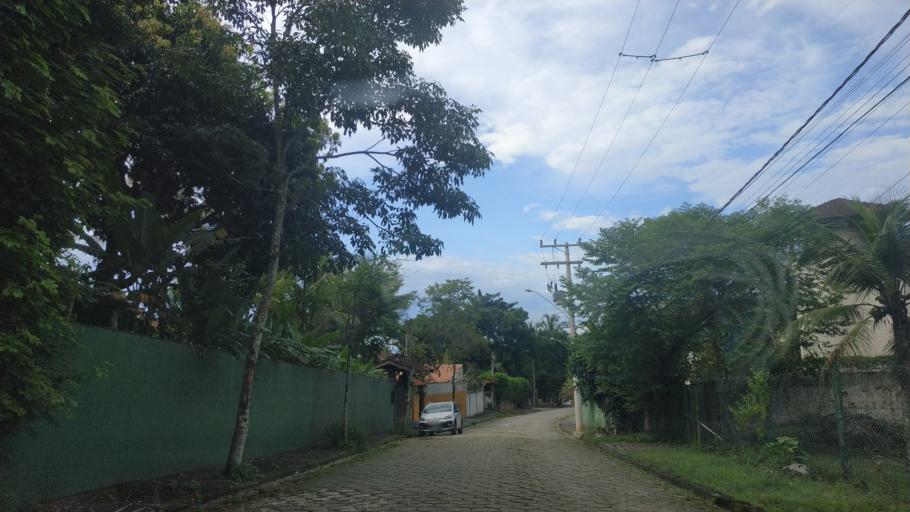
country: BR
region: Sao Paulo
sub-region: Ilhabela
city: Ilhabela
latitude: -23.8303
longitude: -45.3609
